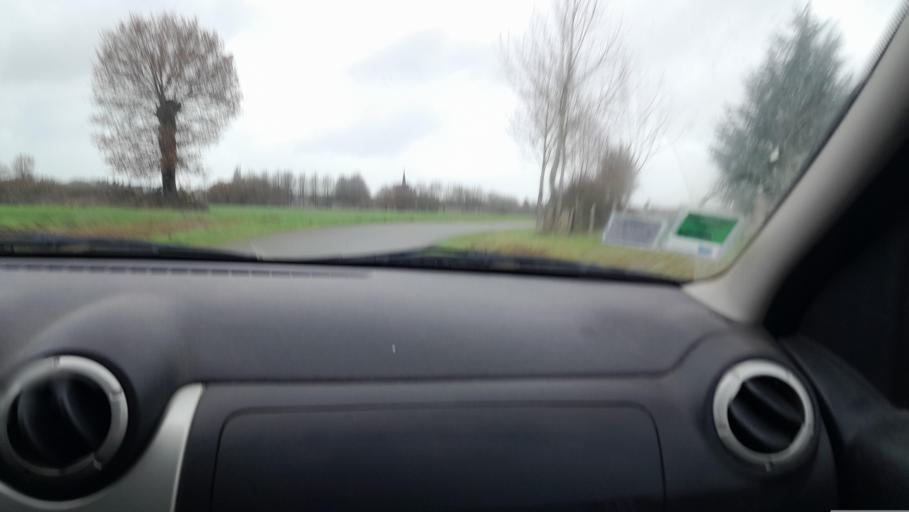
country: FR
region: Pays de la Loire
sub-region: Departement de la Mayenne
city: Ballots
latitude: 47.9033
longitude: -1.1402
